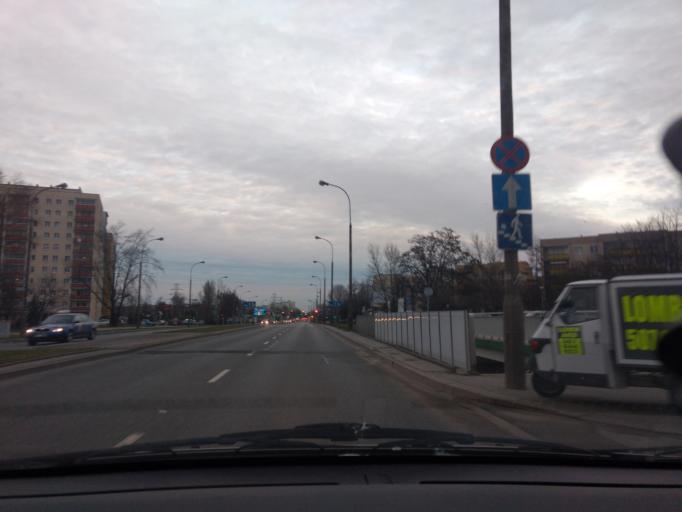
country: PL
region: Masovian Voivodeship
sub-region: Warszawa
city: Praga Poludnie
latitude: 52.2285
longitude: 21.0945
